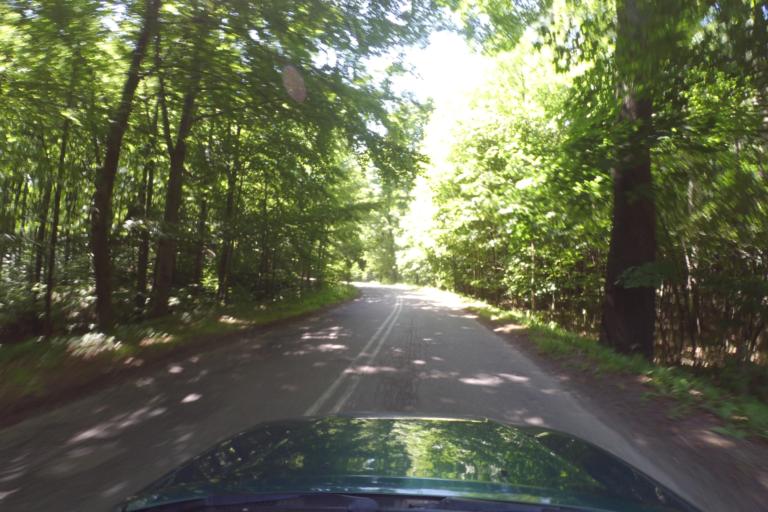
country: PL
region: Lower Silesian Voivodeship
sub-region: Powiat walbrzyski
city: Walbrzych
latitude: 50.7492
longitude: 16.2611
